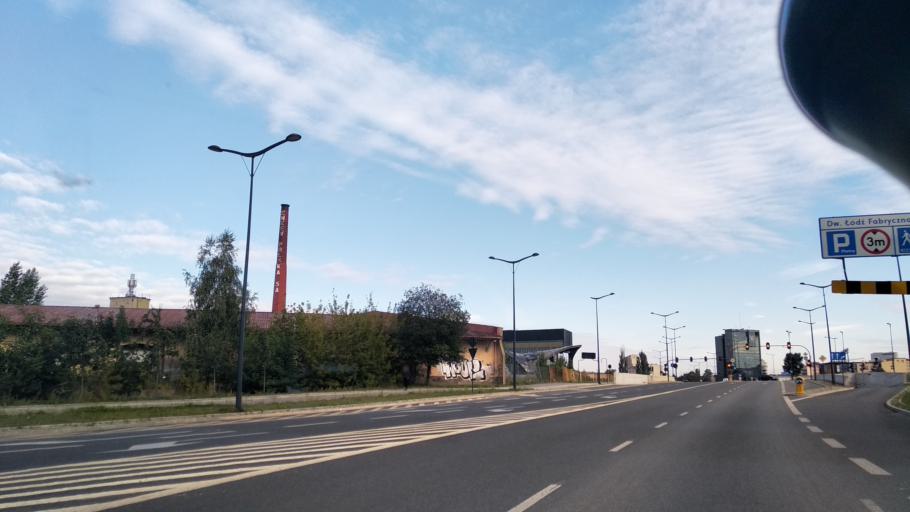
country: PL
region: Lodz Voivodeship
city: Lodz
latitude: 51.7670
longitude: 19.4733
